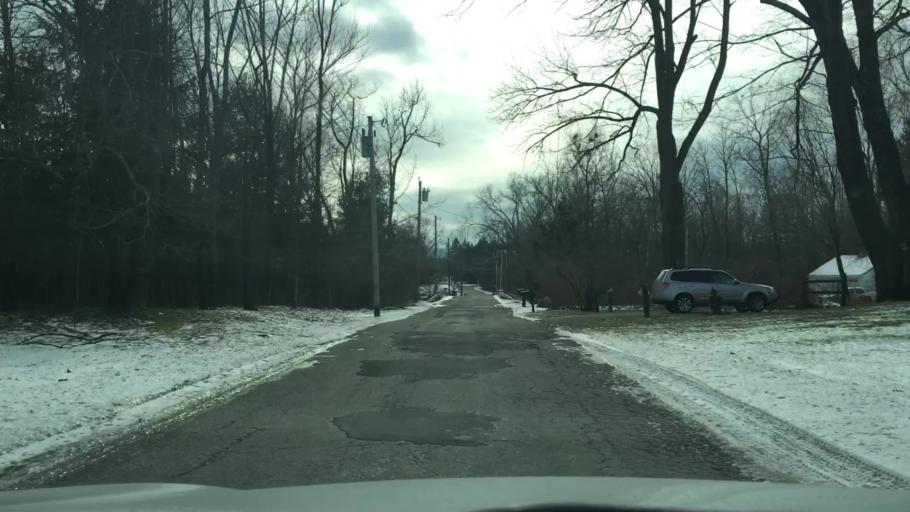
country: US
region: Massachusetts
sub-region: Berkshire County
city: Lee
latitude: 42.3326
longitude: -73.2368
